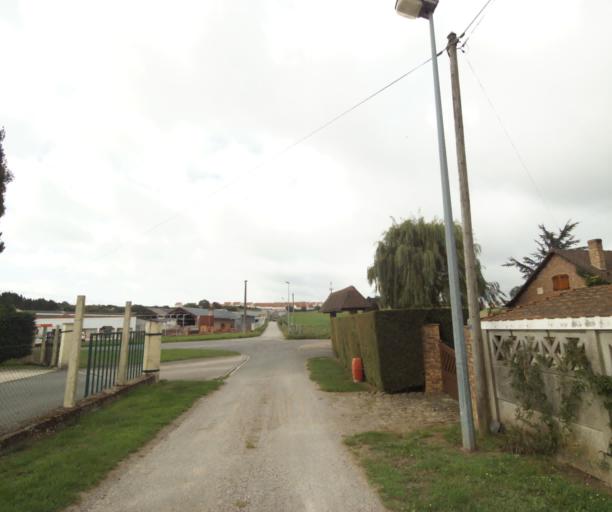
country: FR
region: Nord-Pas-de-Calais
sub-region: Departement du Pas-de-Calais
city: Etaples
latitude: 50.5222
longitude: 1.6602
